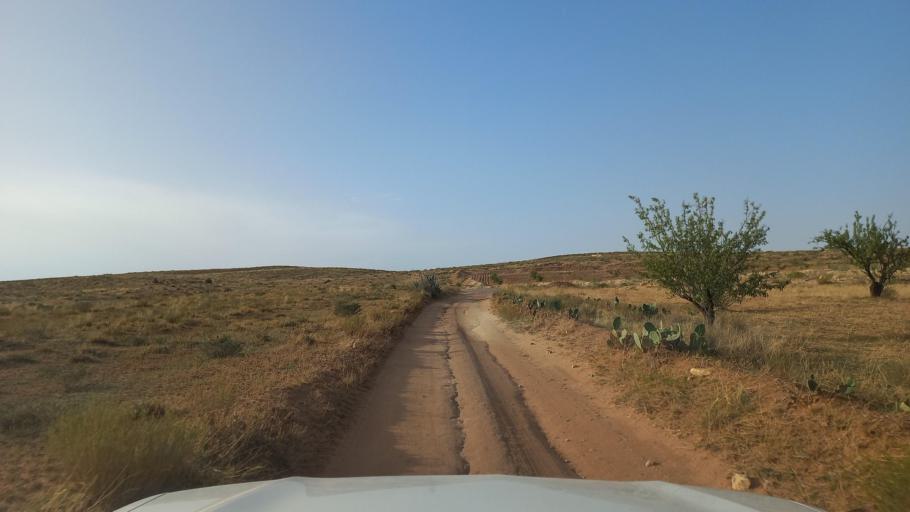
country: TN
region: Al Qasrayn
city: Kasserine
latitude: 35.3597
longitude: 8.8404
